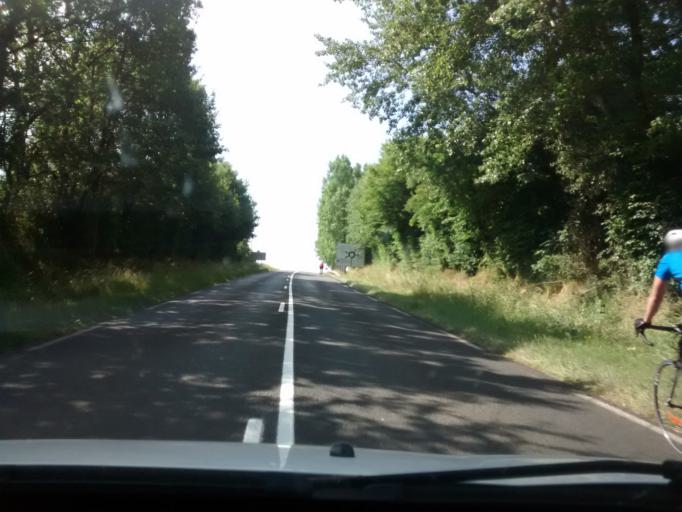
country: FR
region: Pays de la Loire
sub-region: Departement de la Sarthe
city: Vibraye
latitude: 48.0735
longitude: 0.7293
